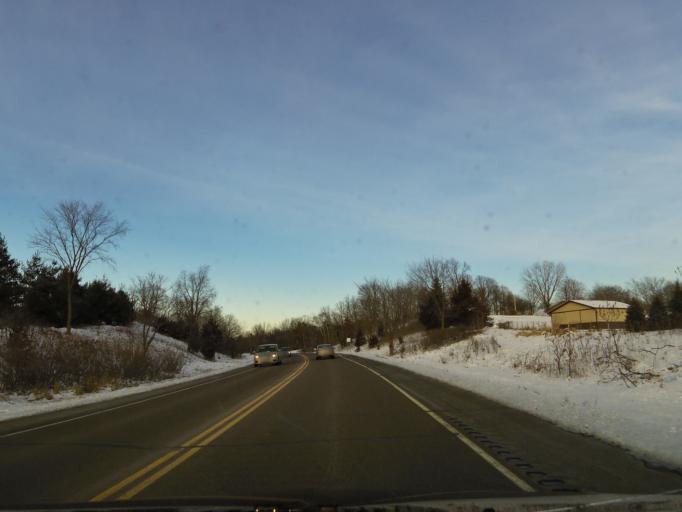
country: US
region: Wisconsin
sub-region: Polk County
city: Osceola
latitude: 45.3268
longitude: -92.7239
